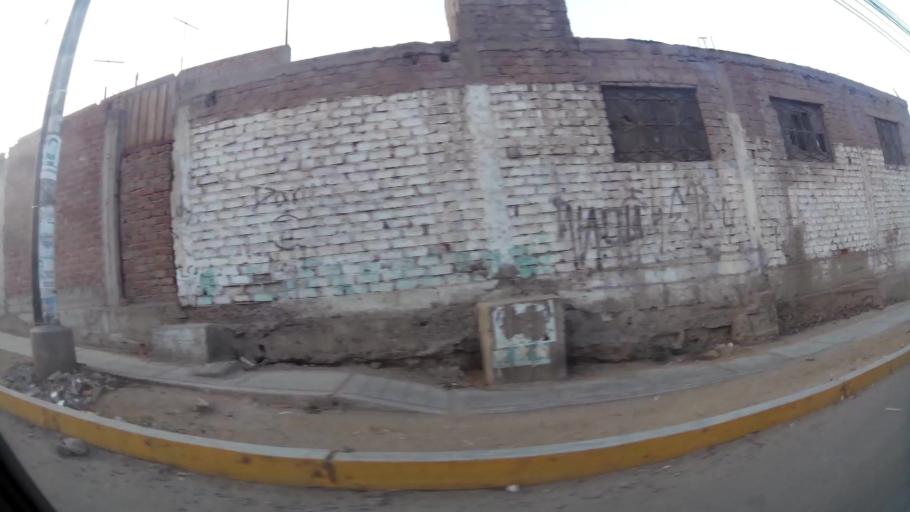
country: PE
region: La Libertad
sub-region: Provincia de Trujillo
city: El Porvenir
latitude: -8.0737
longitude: -78.9980
